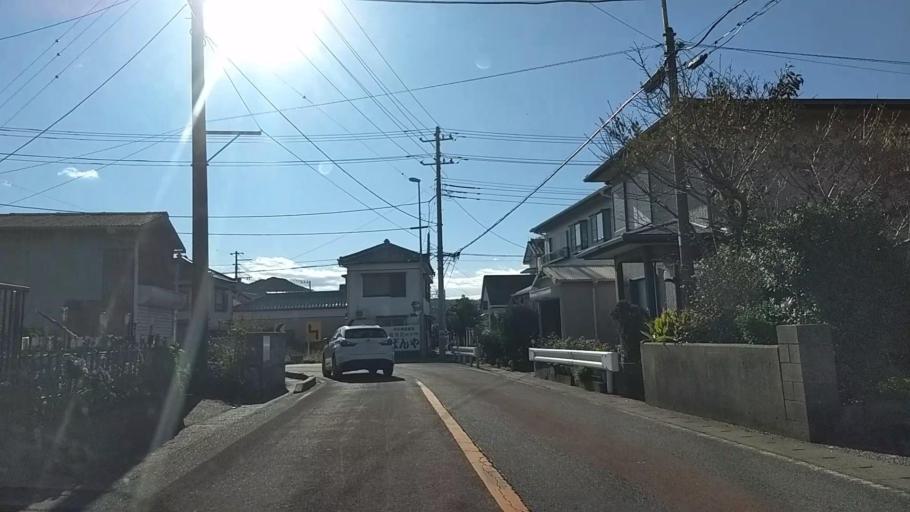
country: JP
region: Chiba
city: Tateyama
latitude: 35.1412
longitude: 139.8364
